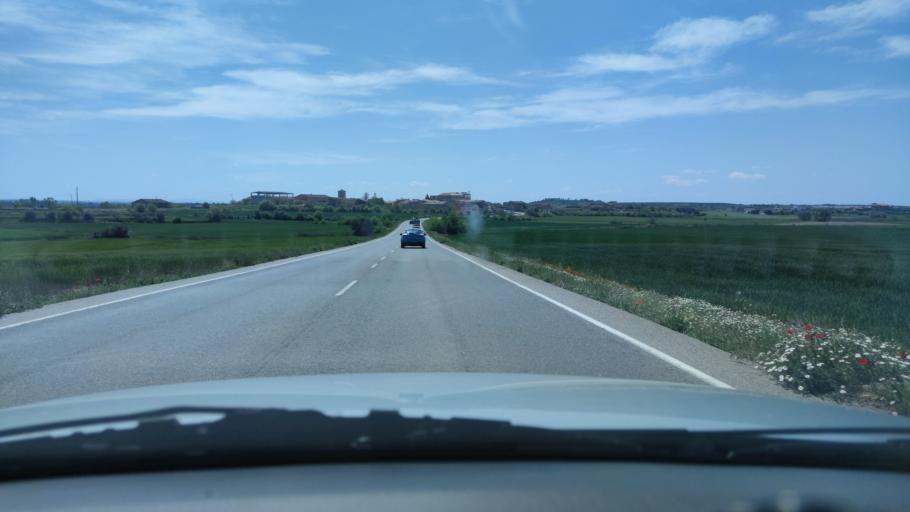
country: ES
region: Catalonia
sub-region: Provincia de Lleida
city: Mont-roig del Camp
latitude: 41.7557
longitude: 1.2402
